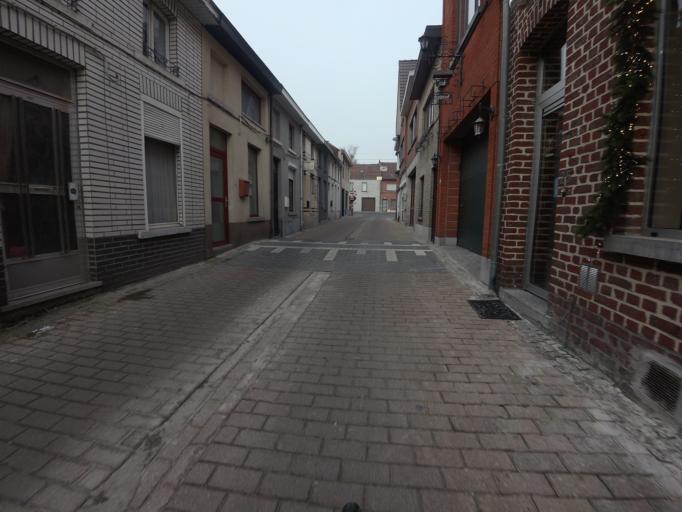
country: BE
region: Flanders
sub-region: Provincie Oost-Vlaanderen
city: Ninove
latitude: 50.8372
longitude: 4.0167
